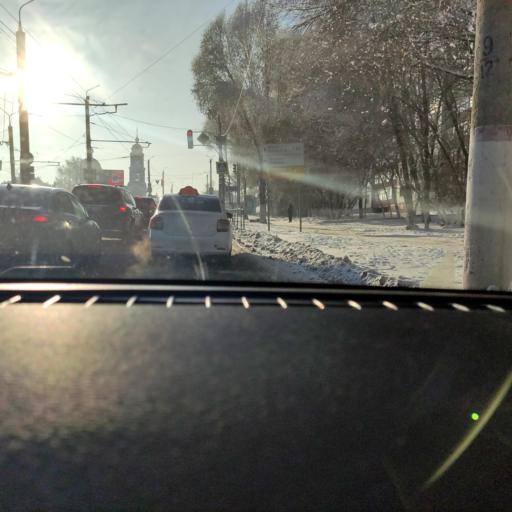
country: RU
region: Samara
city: Novokuybyshevsk
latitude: 53.1046
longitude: 49.9550
